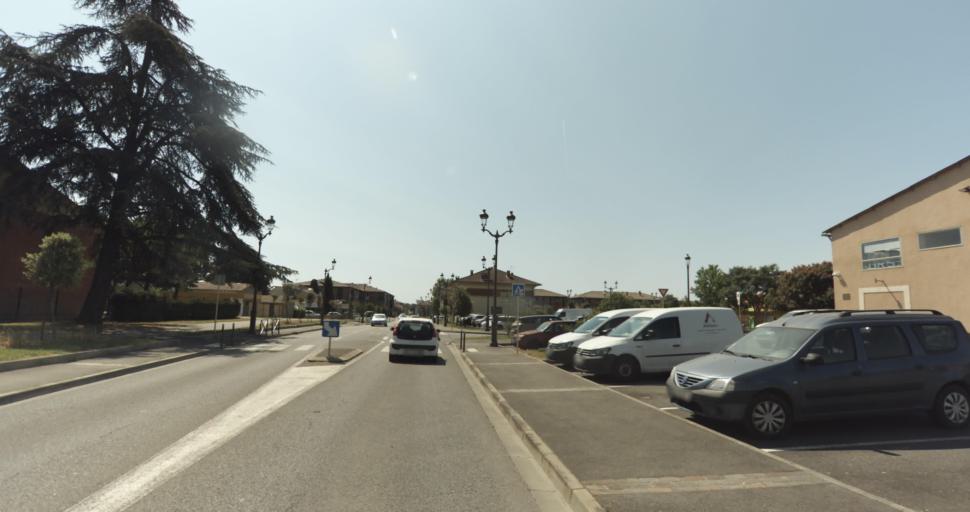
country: FR
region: Midi-Pyrenees
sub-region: Departement de la Haute-Garonne
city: Plaisance-du-Touch
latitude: 43.5685
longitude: 1.2958
